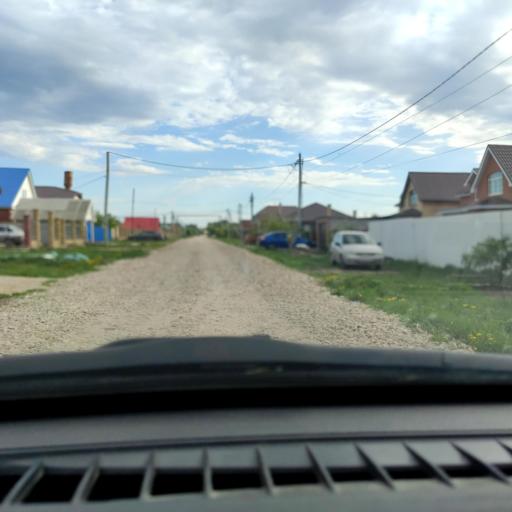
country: RU
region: Samara
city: Tol'yatti
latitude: 53.5645
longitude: 49.4073
